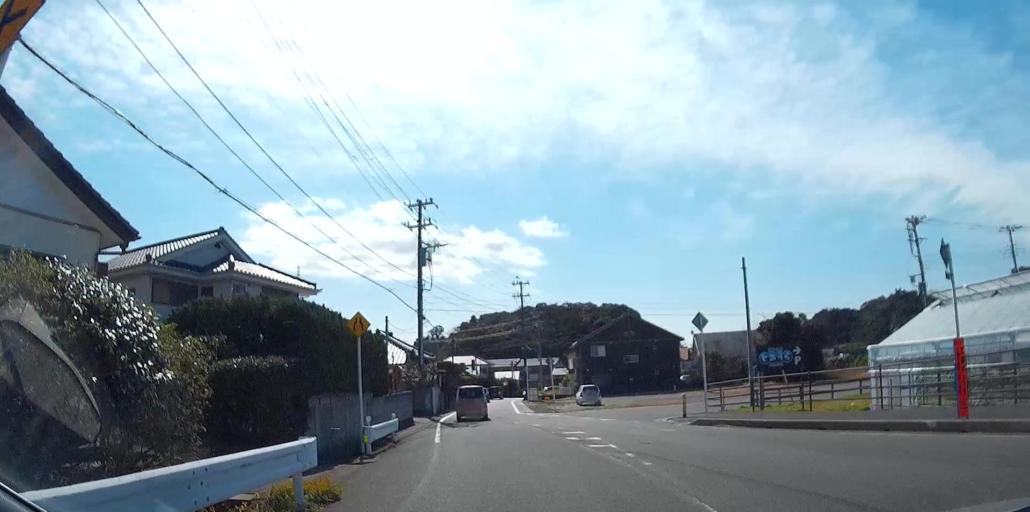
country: JP
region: Chiba
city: Tateyama
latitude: 35.0363
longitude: 139.8510
